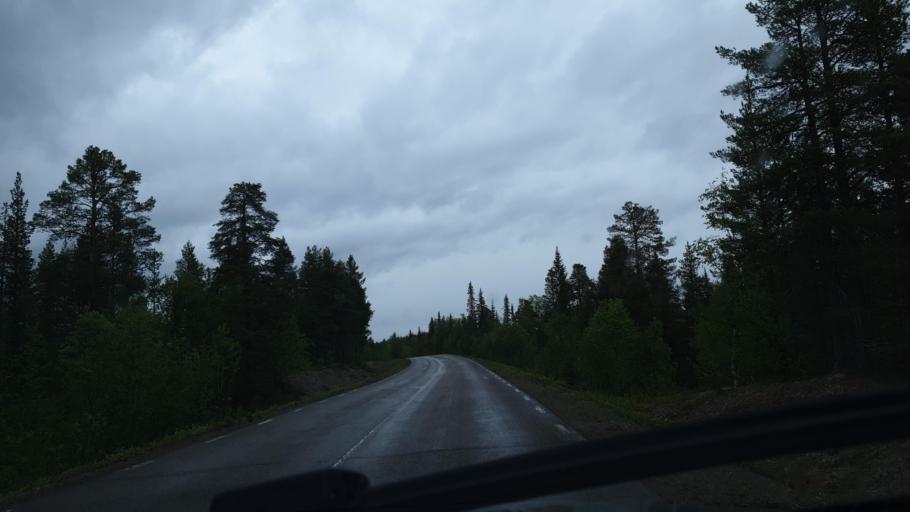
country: SE
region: Norrbotten
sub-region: Kiruna Kommun
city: Kiruna
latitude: 67.8845
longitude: 21.0080
